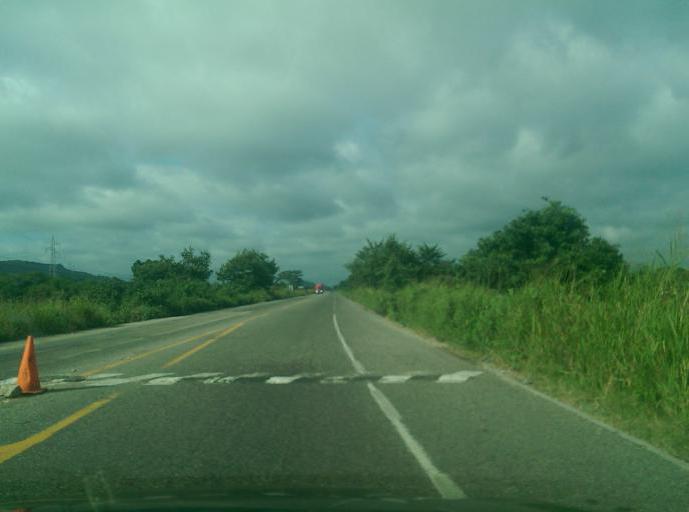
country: MX
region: Tabasco
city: Aquiles Serdan
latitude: 17.6930
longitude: -92.3165
